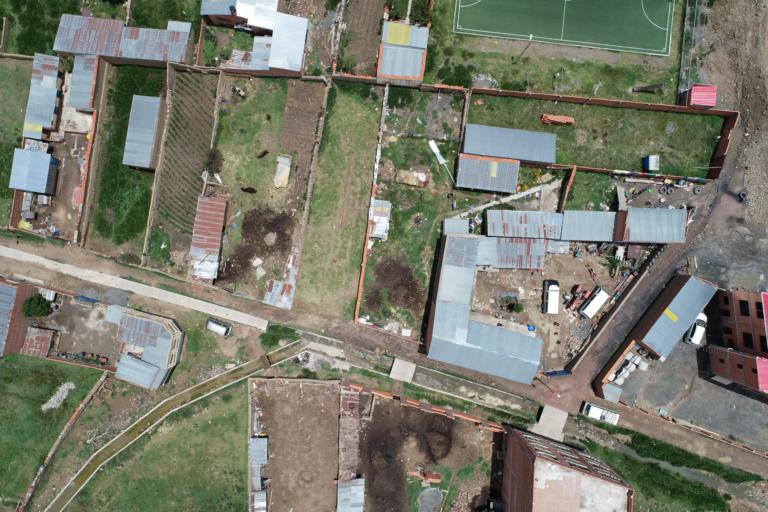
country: BO
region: La Paz
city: Huarina
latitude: -16.1907
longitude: -68.6040
